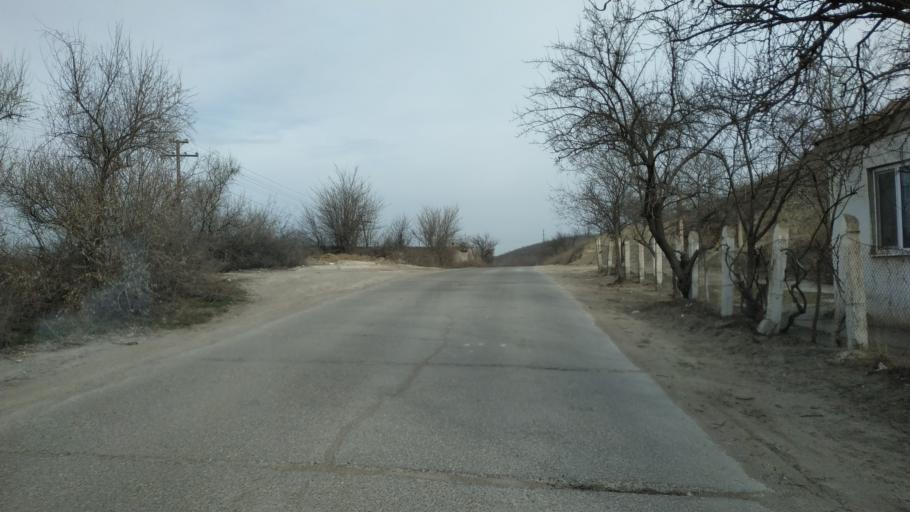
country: MD
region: Chisinau
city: Vatra
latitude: 47.0793
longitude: 28.7416
